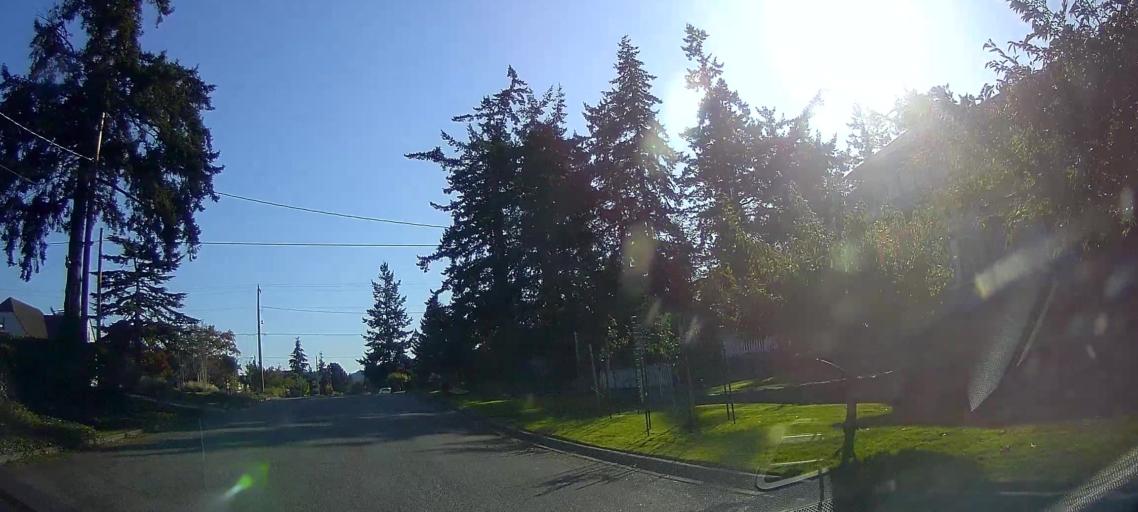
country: US
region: Washington
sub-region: Skagit County
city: Anacortes
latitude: 48.5158
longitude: -122.6235
